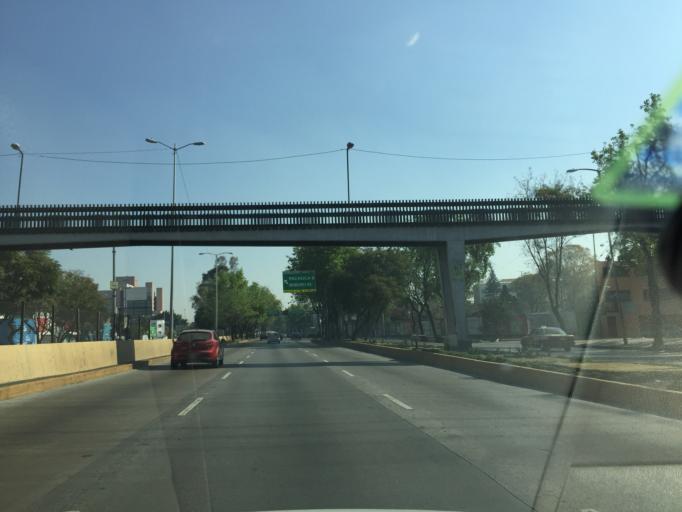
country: MX
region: Mexico City
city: Cuauhtemoc
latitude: 19.4633
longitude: -99.1486
